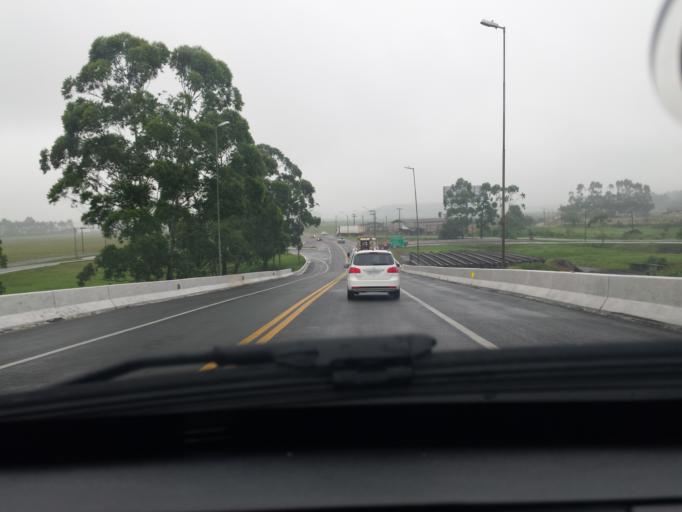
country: BR
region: Santa Catarina
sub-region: Navegantes
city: Navegantes
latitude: -26.8412
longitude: -48.7163
